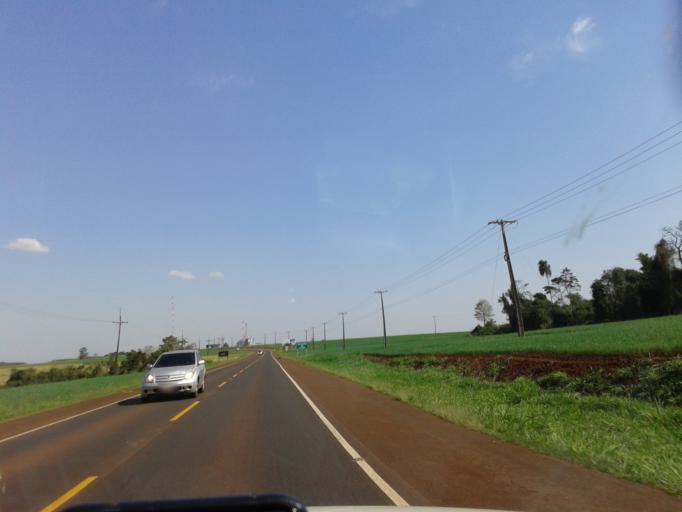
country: PY
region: Alto Parana
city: Santa Rita
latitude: -25.6306
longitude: -54.9686
